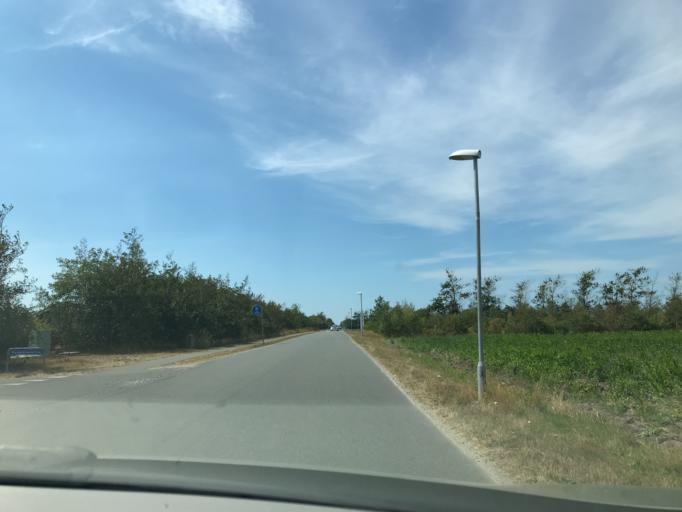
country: DK
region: Central Jutland
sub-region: Ringkobing-Skjern Kommune
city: Skjern
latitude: 55.8902
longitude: 8.3771
